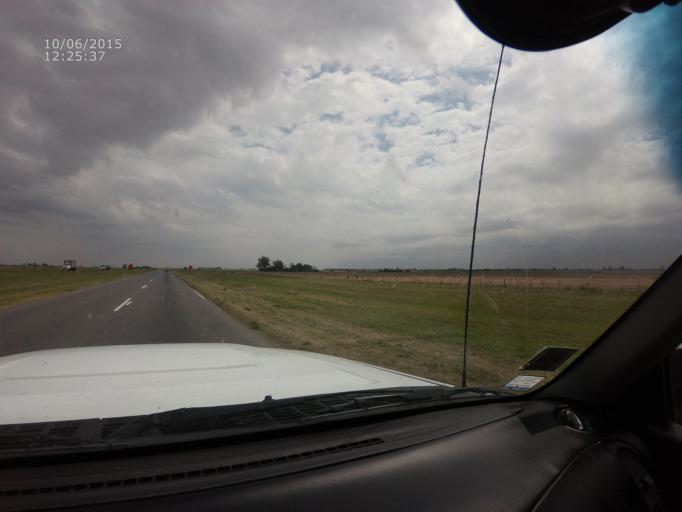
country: AR
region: Santa Fe
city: Roldan
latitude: -32.9061
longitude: -61.0017
